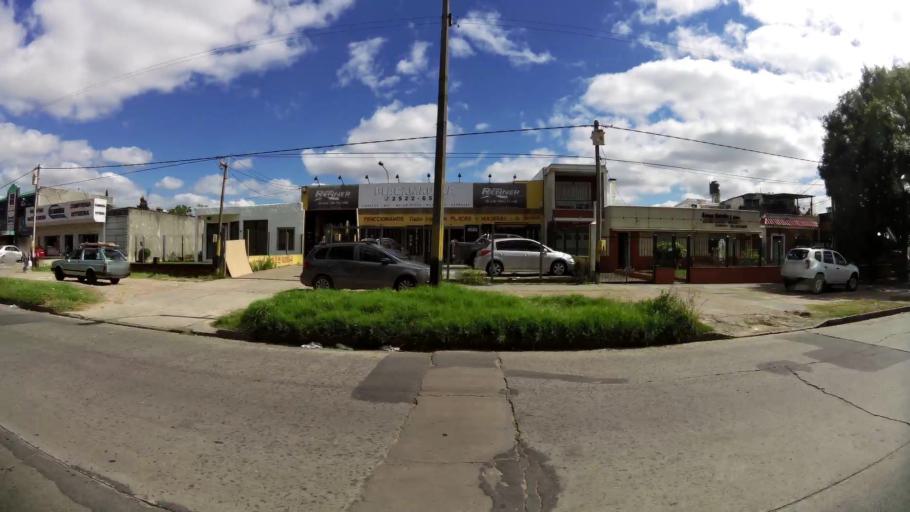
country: UY
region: Canelones
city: Paso de Carrasco
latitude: -34.8721
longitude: -56.1199
